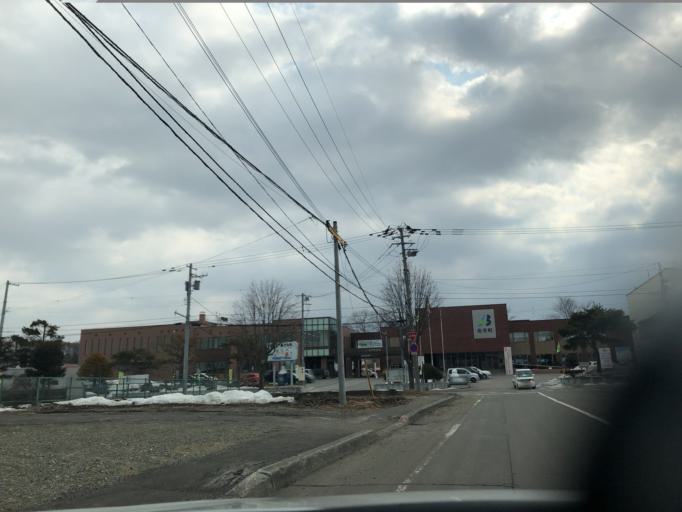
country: JP
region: Hokkaido
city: Chitose
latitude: 42.7635
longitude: 141.8171
